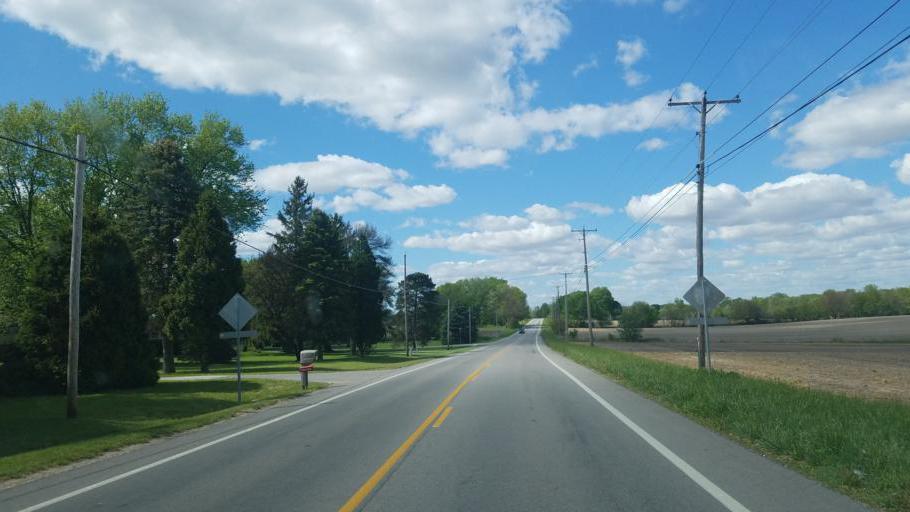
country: US
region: Ohio
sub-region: Marion County
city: Marion
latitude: 40.5210
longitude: -83.1006
